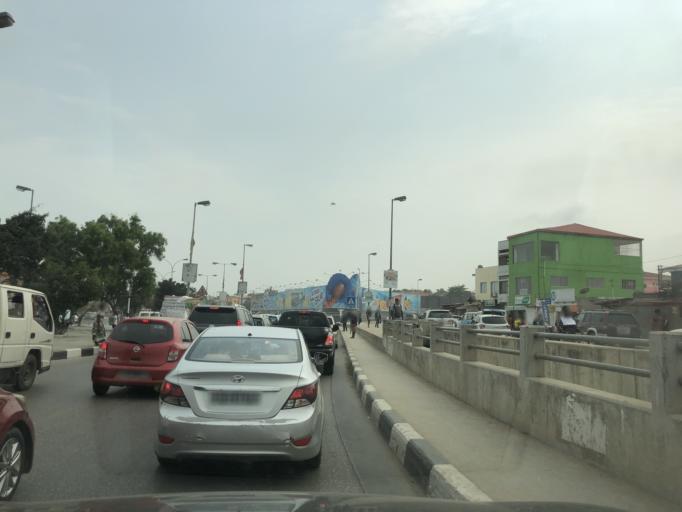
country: AO
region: Luanda
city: Luanda
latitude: -8.8488
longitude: 13.2110
